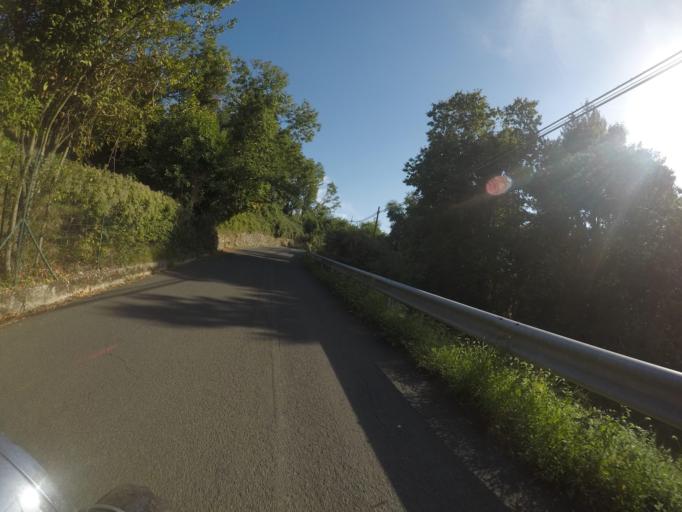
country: IT
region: Tuscany
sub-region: Provincia di Massa-Carrara
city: Massa
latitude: 44.0720
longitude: 10.1146
